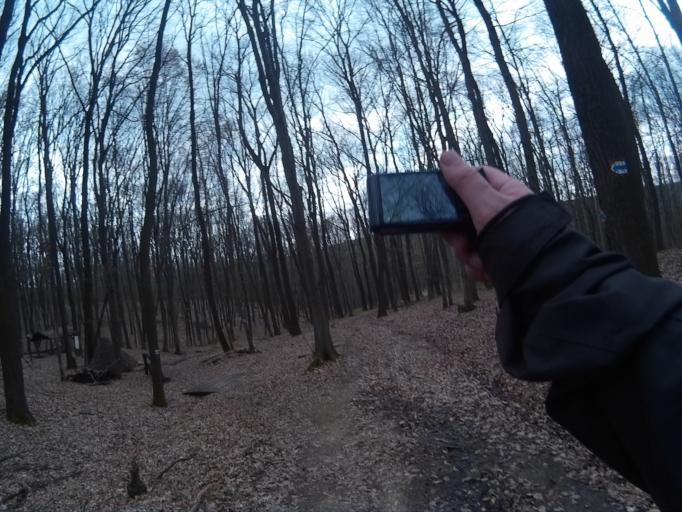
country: HU
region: Pest
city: Kosd
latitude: 47.8427
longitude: 19.1308
